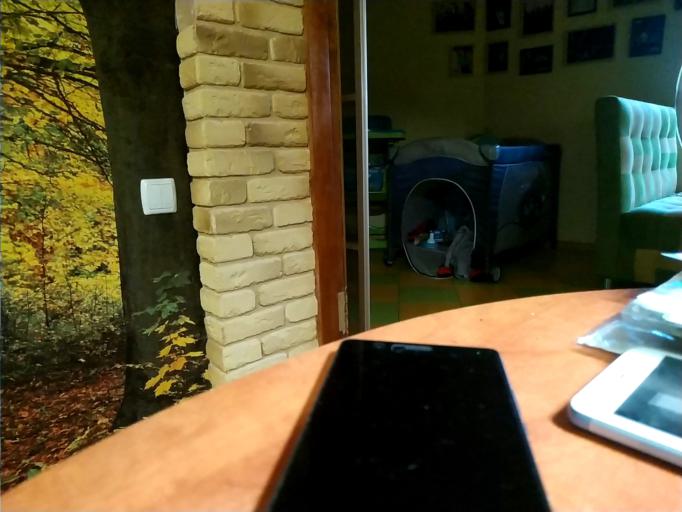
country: RU
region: Orjol
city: Znamenskoye
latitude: 53.4822
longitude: 35.5141
